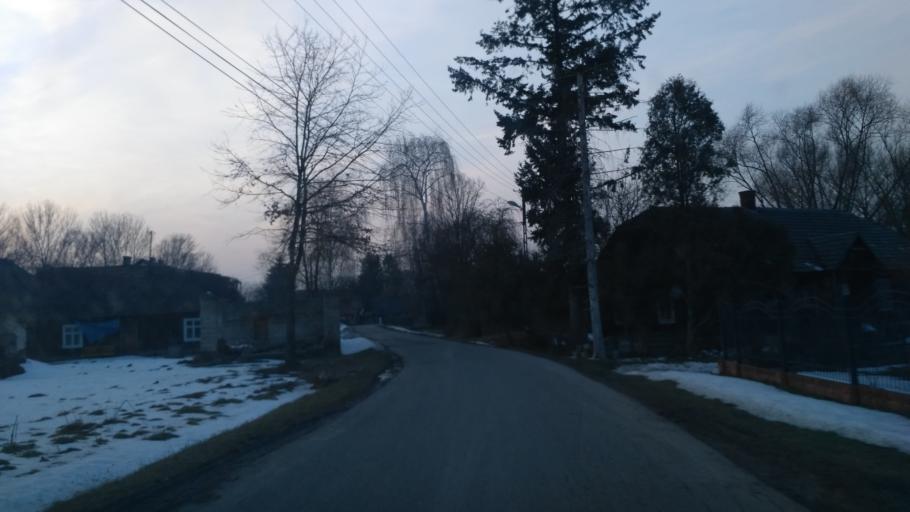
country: PL
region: Subcarpathian Voivodeship
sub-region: Powiat rzeszowski
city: Siedliska
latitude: 49.9676
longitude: 21.9682
